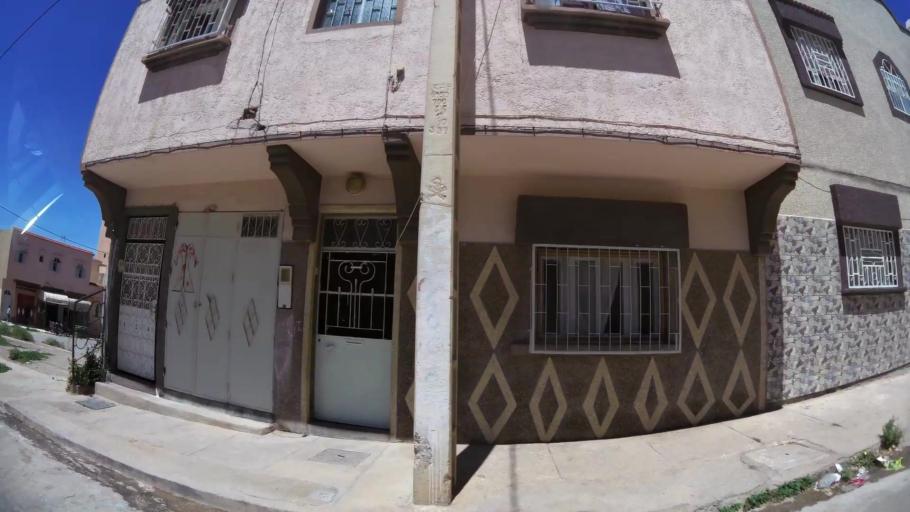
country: MA
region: Oriental
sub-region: Oujda-Angad
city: Oujda
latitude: 34.6580
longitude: -1.9293
